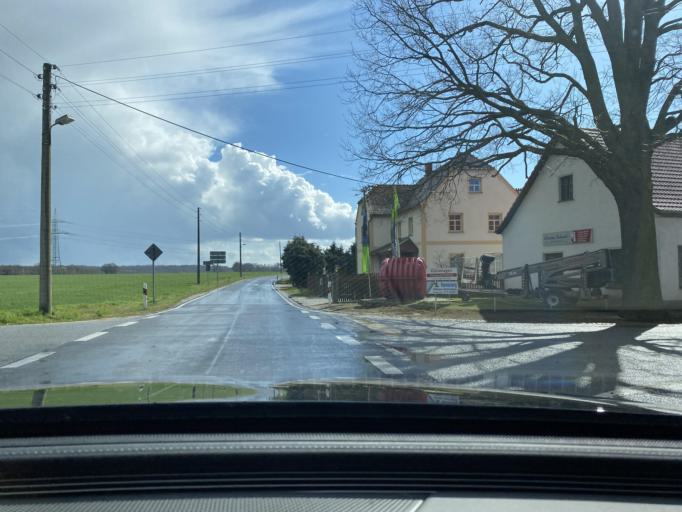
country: DE
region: Saxony
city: Grossdubrau
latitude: 51.2728
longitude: 14.4318
